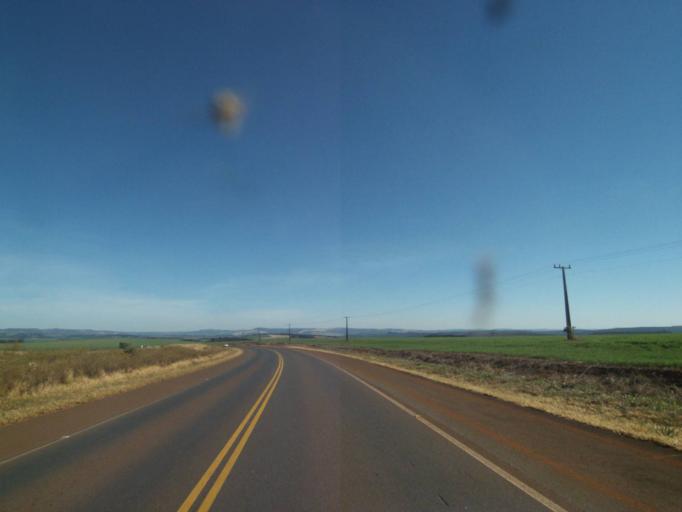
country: BR
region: Parana
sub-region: Tibagi
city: Tibagi
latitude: -24.4366
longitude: -50.4204
